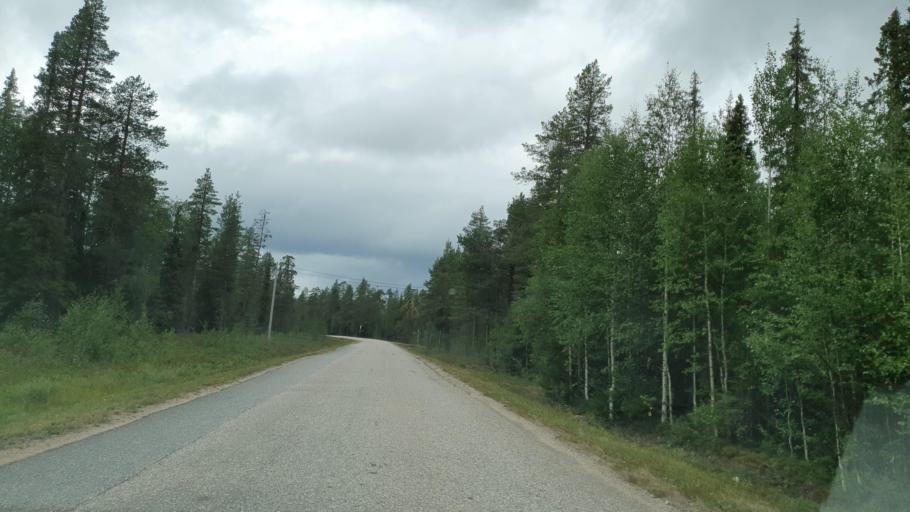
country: FI
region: Lapland
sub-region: Tunturi-Lappi
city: Kolari
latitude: 67.5217
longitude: 24.1795
